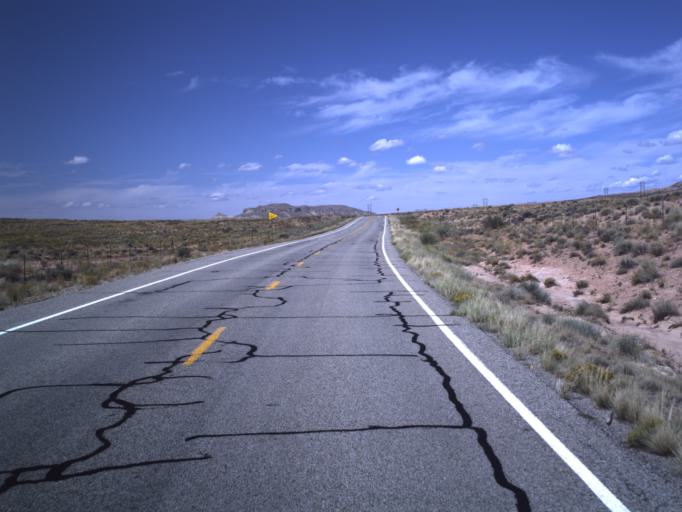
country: US
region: Utah
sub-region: San Juan County
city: Blanding
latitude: 37.2927
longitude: -109.4205
